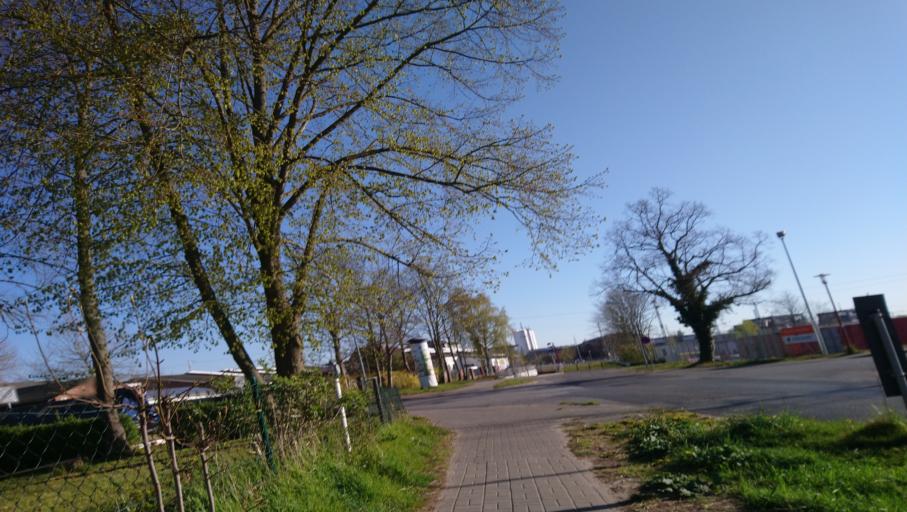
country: DE
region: Mecklenburg-Vorpommern
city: Rostock
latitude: 54.0720
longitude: 12.1370
